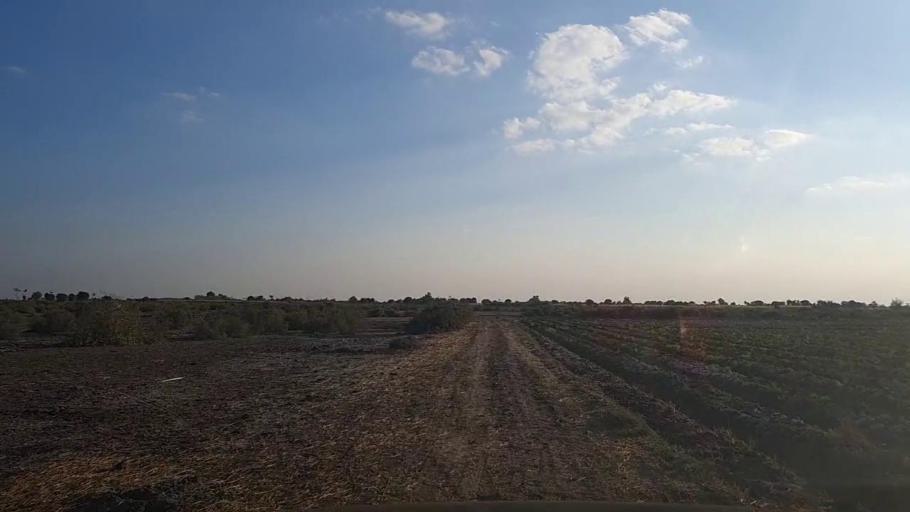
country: PK
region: Sindh
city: Tando Mittha Khan
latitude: 25.9194
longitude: 69.0606
